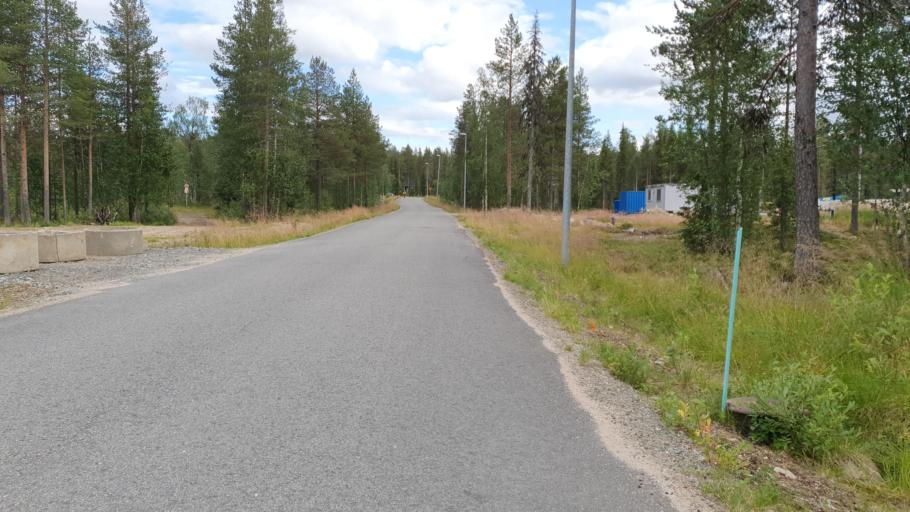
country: FI
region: Lapland
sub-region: Tunturi-Lappi
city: Kolari
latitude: 67.5976
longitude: 24.1392
